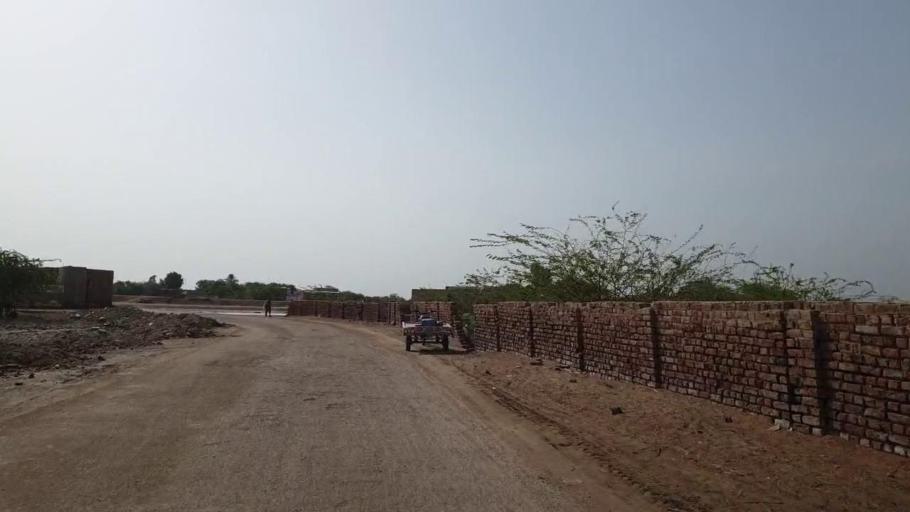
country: PK
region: Sindh
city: Jam Sahib
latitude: 26.2977
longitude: 68.6345
